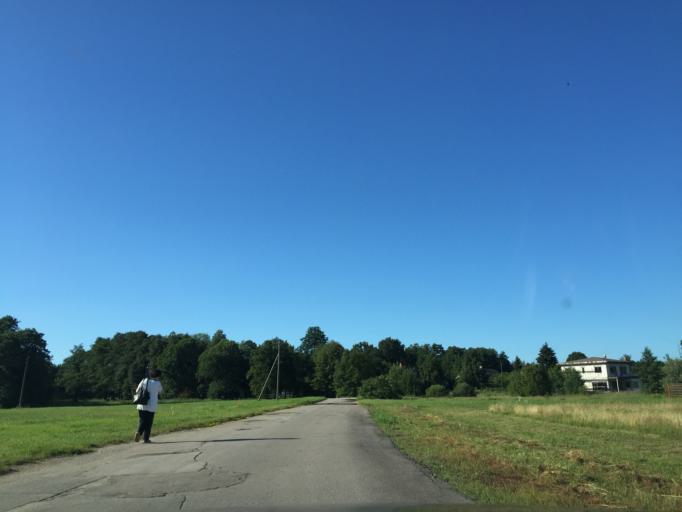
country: LV
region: Riga
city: Jaunciems
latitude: 57.0609
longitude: 24.1384
